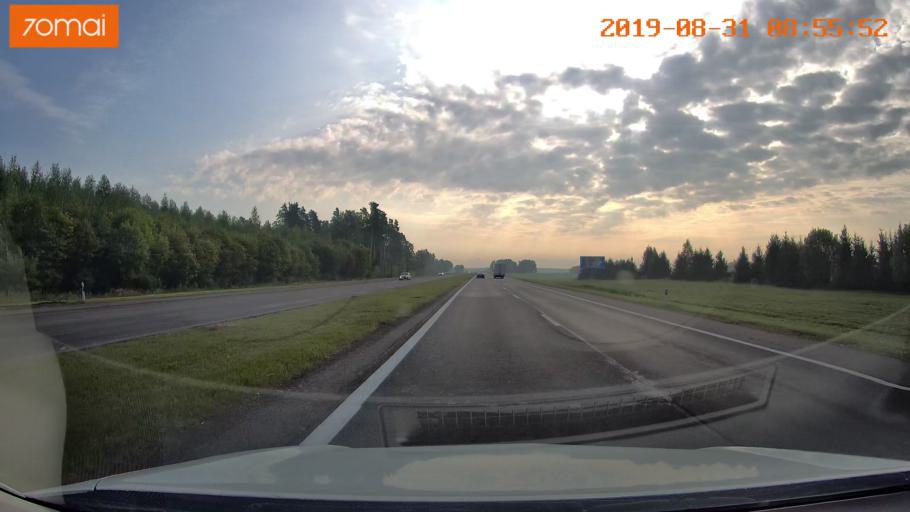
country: BY
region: Minsk
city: Smilavichy
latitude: 53.7648
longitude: 28.1176
